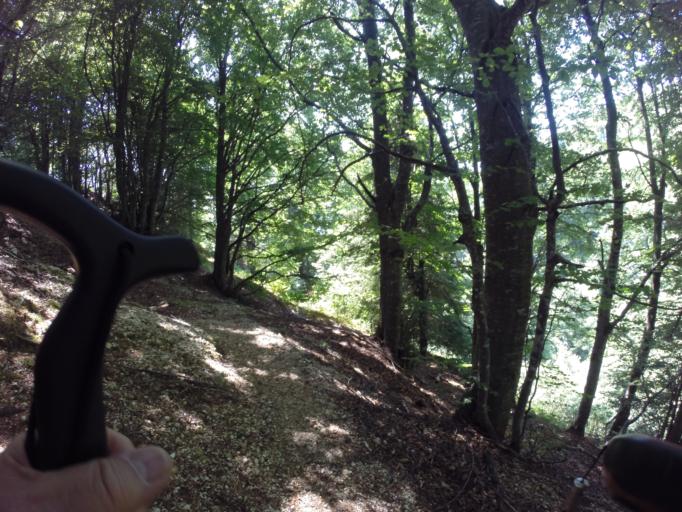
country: IT
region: Veneto
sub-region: Provincia di Treviso
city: Crespano del Grappa
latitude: 45.9058
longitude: 11.8284
